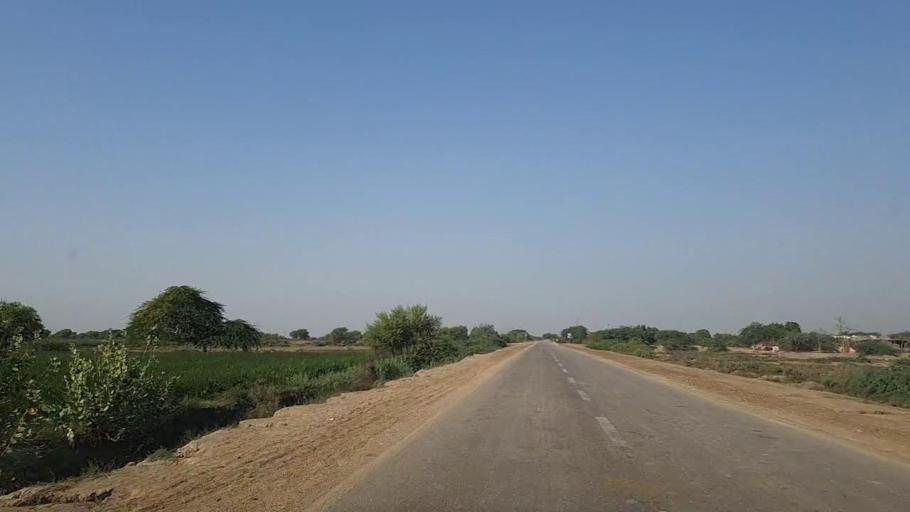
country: PK
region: Sindh
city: Mirpur Batoro
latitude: 24.5720
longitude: 68.3938
